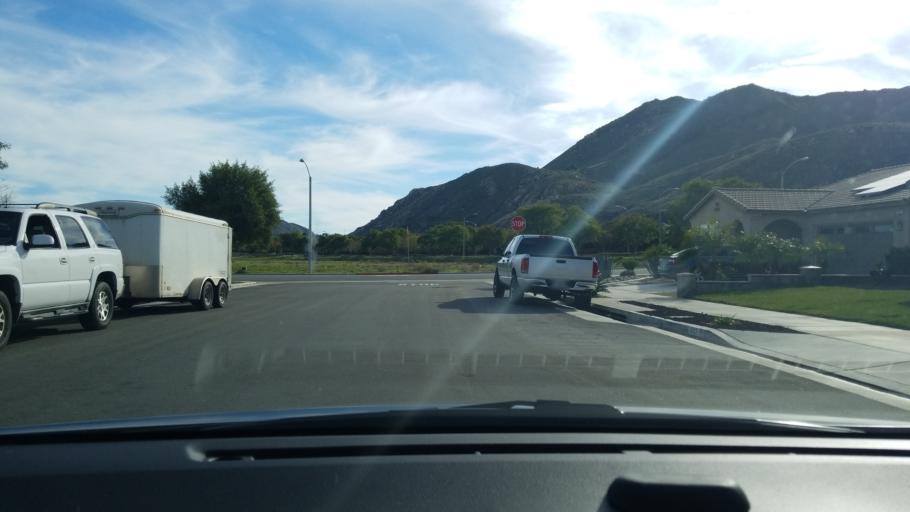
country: US
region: California
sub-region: Riverside County
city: Green Acres
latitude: 33.7933
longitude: -117.0373
